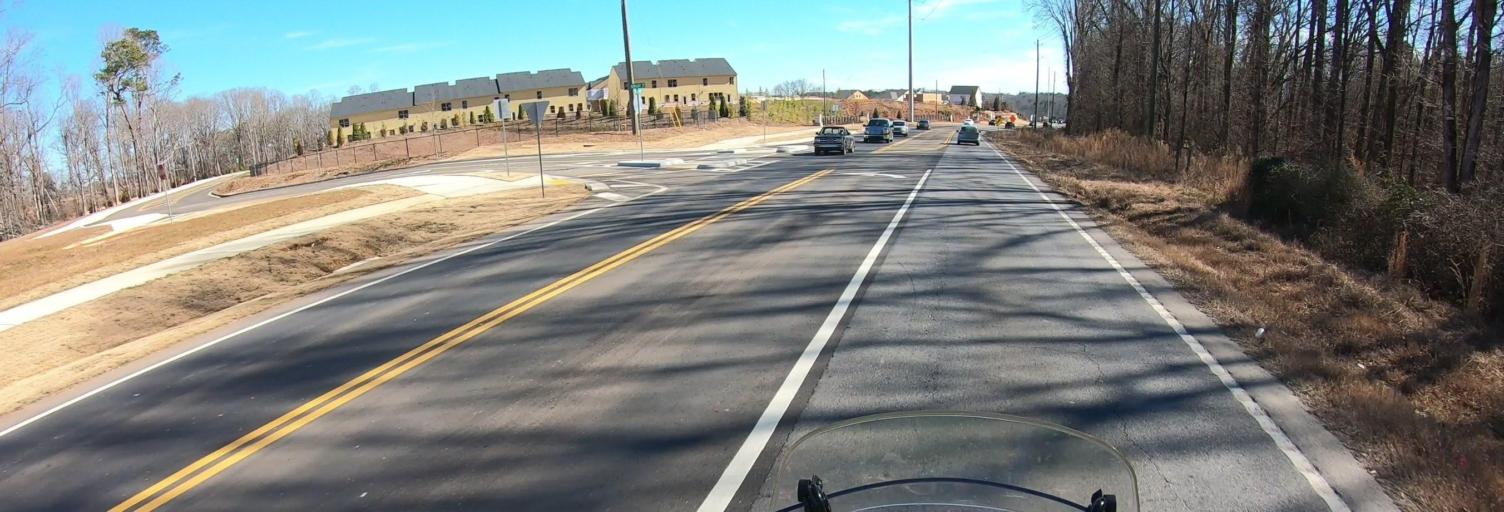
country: US
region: Georgia
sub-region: Forsyth County
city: Cumming
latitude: 34.2931
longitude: -84.1520
